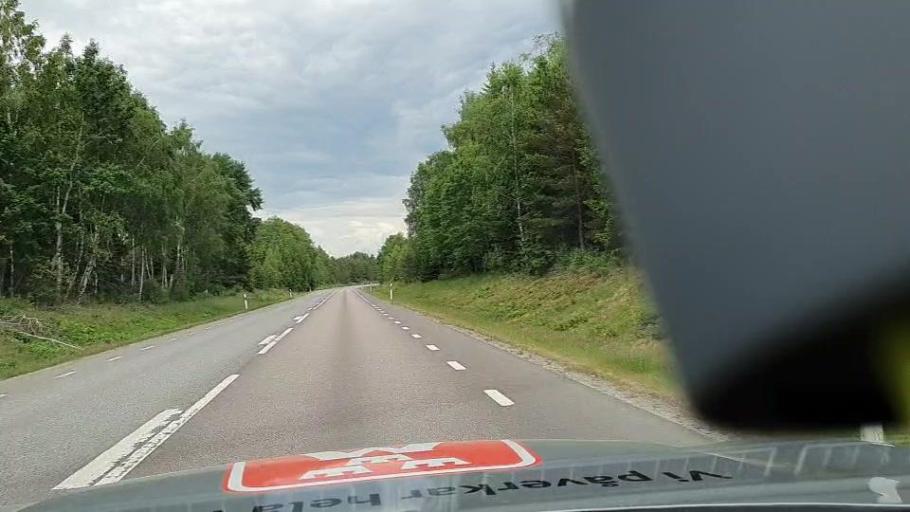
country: SE
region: Kalmar
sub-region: Emmaboda Kommun
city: Emmaboda
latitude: 56.4483
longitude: 15.5634
